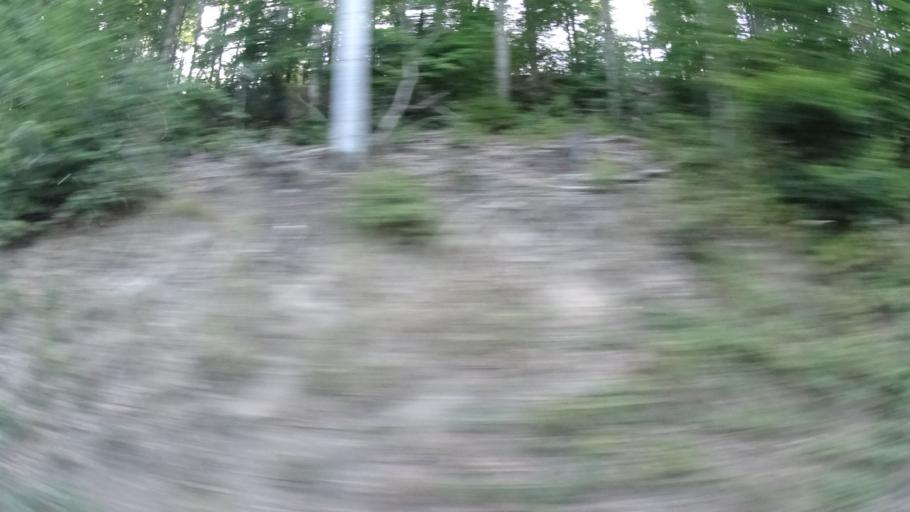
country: DE
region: Hesse
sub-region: Regierungsbezirk Darmstadt
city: Gelnhausen
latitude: 50.2710
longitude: 9.2178
